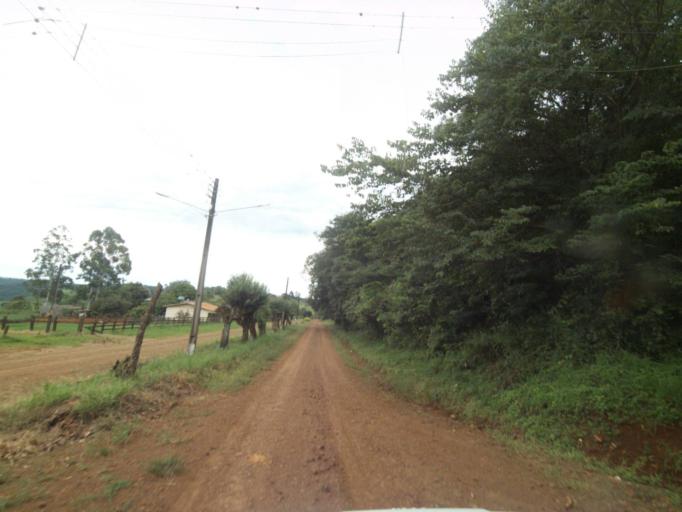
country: BR
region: Parana
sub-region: Guaraniacu
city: Guaraniacu
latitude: -24.9162
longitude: -52.9377
